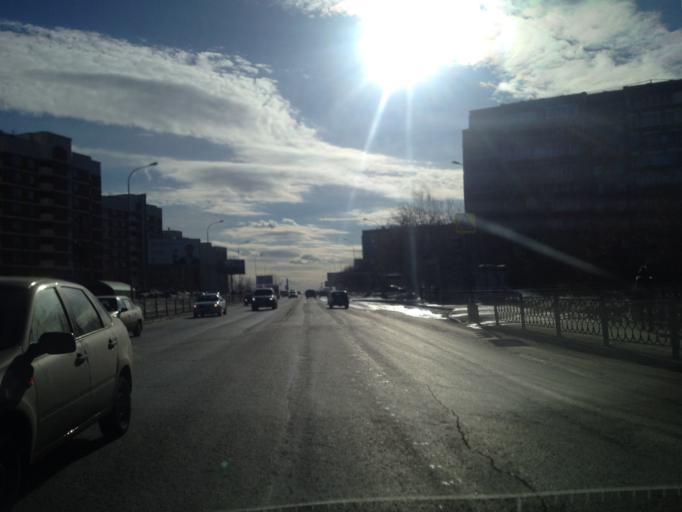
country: RU
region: Sverdlovsk
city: Yekaterinburg
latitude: 56.8521
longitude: 60.5705
